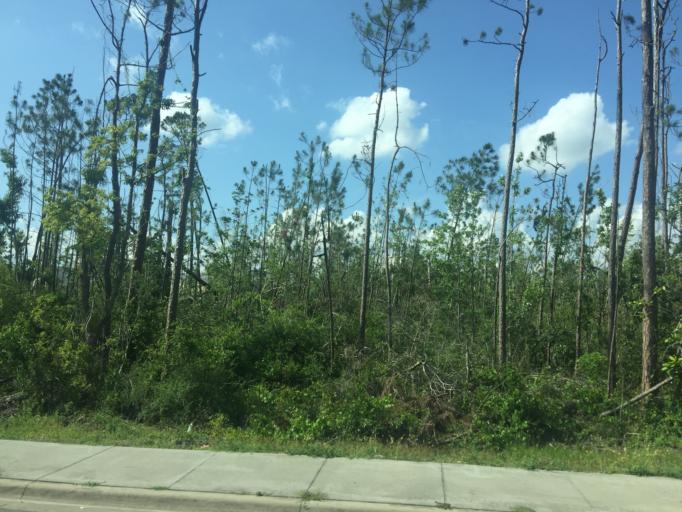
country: US
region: Florida
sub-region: Bay County
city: Cedar Grove
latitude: 30.1676
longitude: -85.6281
